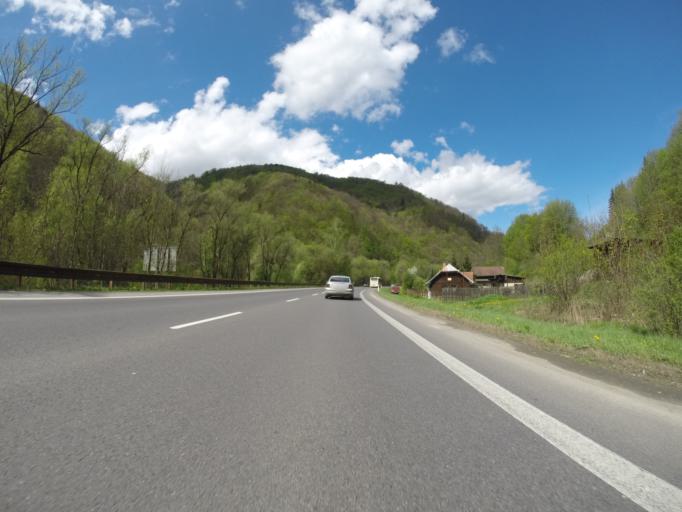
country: SK
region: Banskobystricky
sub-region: Okres Banska Bystrica
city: Brezno
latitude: 48.8025
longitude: 19.5523
